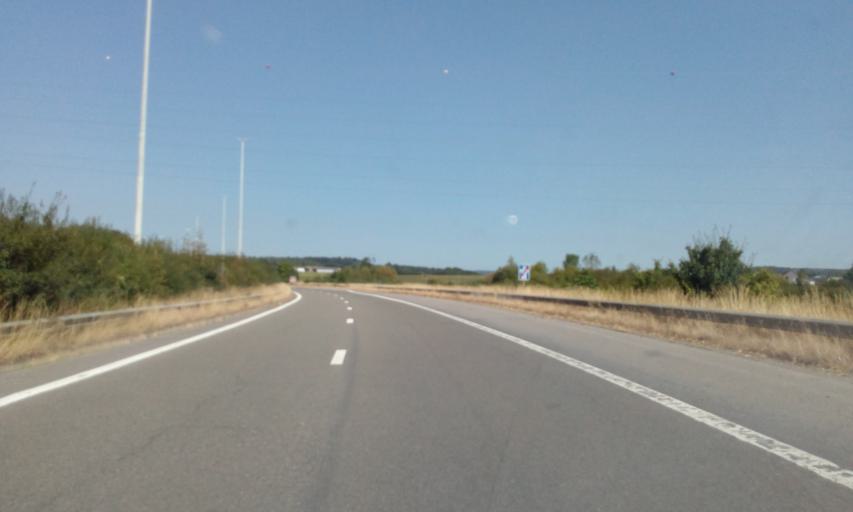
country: BE
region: Wallonia
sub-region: Province du Luxembourg
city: Aubange
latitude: 49.5726
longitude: 5.8214
